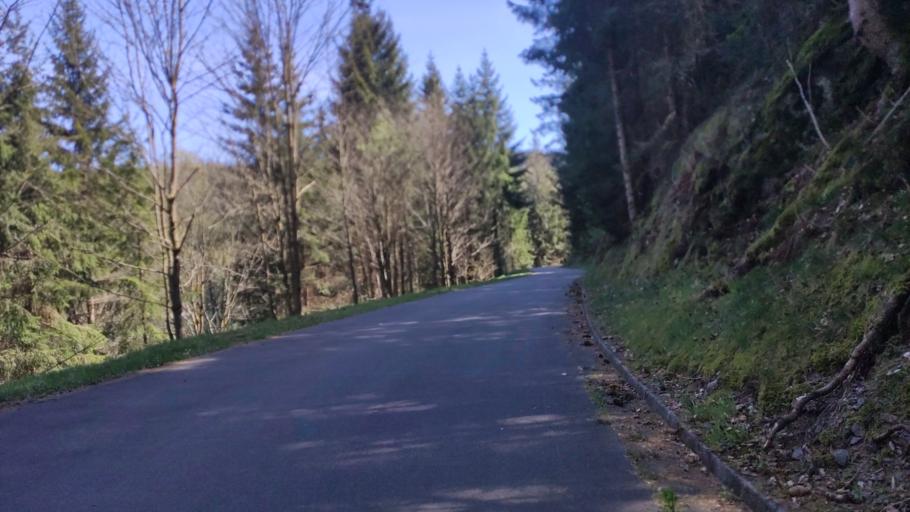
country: DE
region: Bavaria
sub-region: Upper Franconia
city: Nordhalben
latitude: 50.3440
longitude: 11.4862
